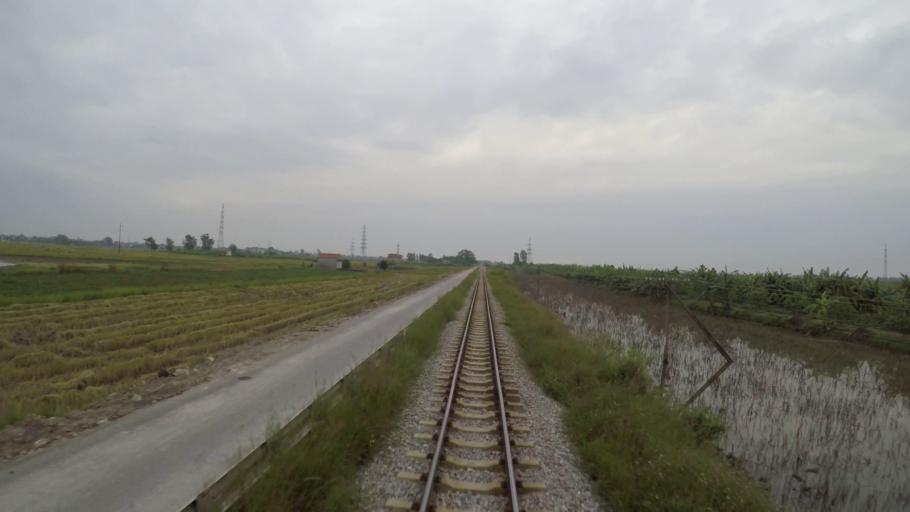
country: VN
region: Hai Duong
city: Ke Sat
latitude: 20.9656
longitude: 106.1223
